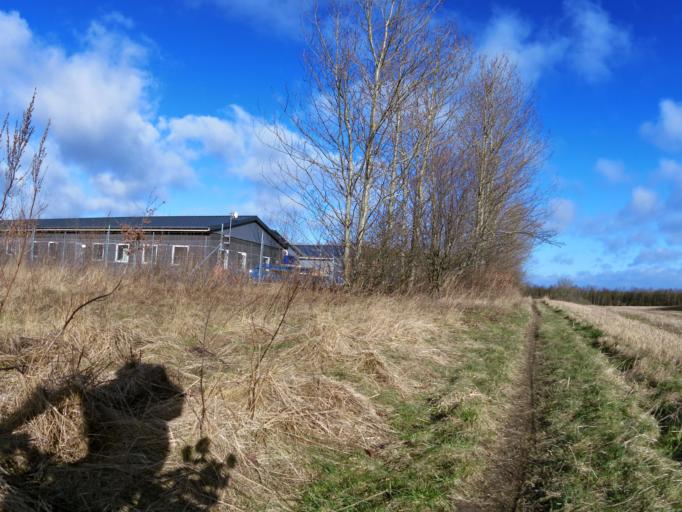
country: DK
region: Central Jutland
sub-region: Arhus Kommune
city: Tranbjerg
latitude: 56.1032
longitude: 10.1252
